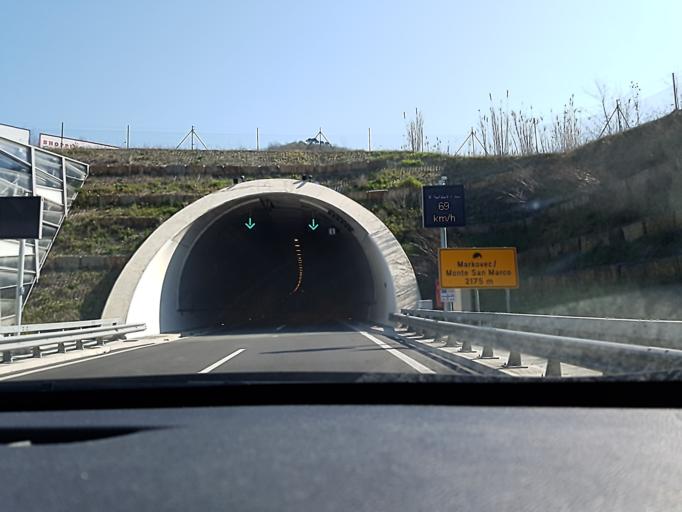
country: SI
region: Izola-Isola
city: Izola
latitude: 45.5391
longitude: 13.6889
